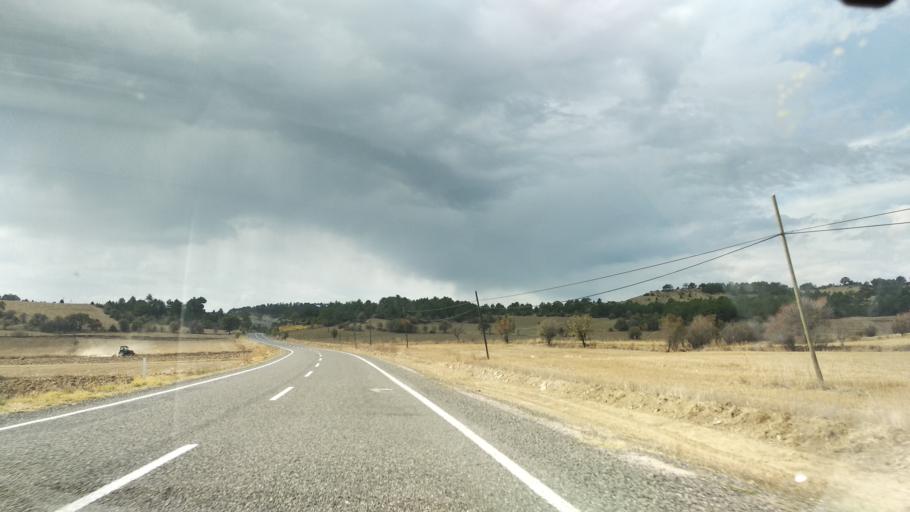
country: TR
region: Bolu
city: Seben
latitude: 40.3619
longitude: 31.4935
